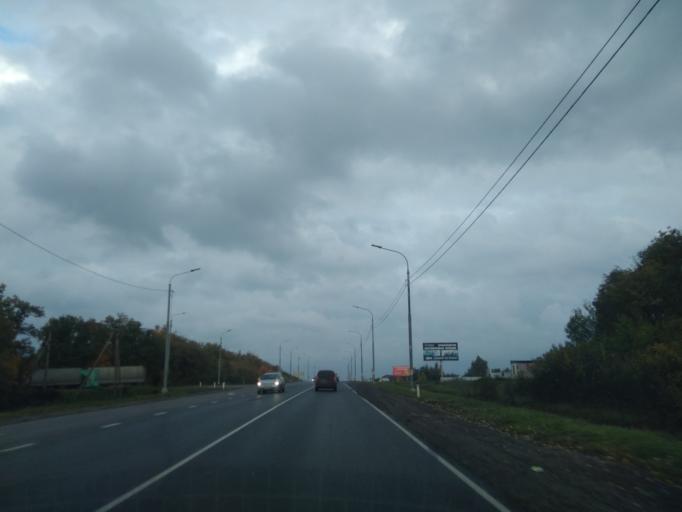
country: RU
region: Lipetsk
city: Syrskoye
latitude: 52.6032
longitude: 39.3620
